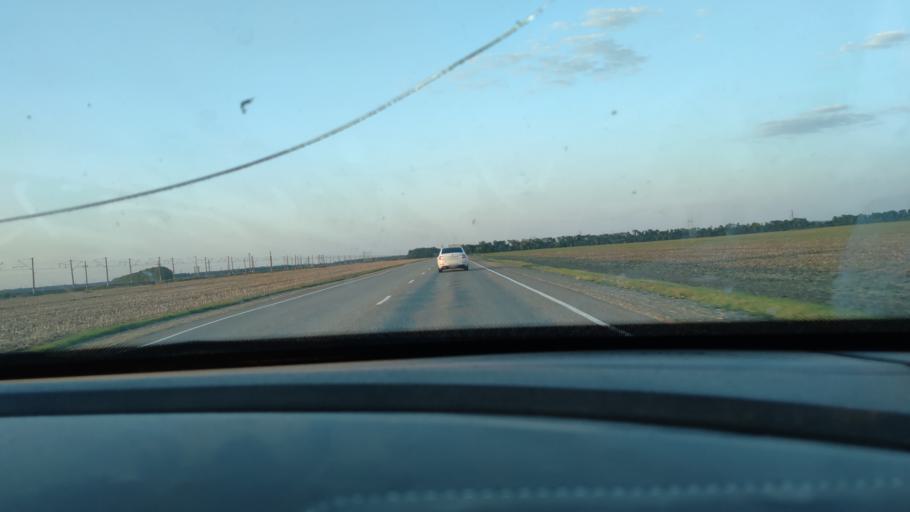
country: RU
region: Krasnodarskiy
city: Novominskaya
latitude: 46.3852
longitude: 38.9858
